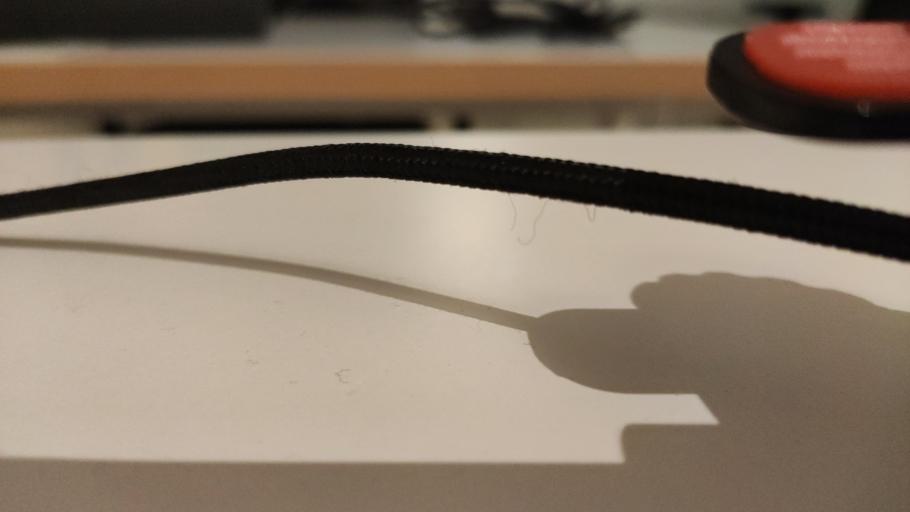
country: RU
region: Moskovskaya
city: Rybnoye
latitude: 56.4004
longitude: 37.6398
